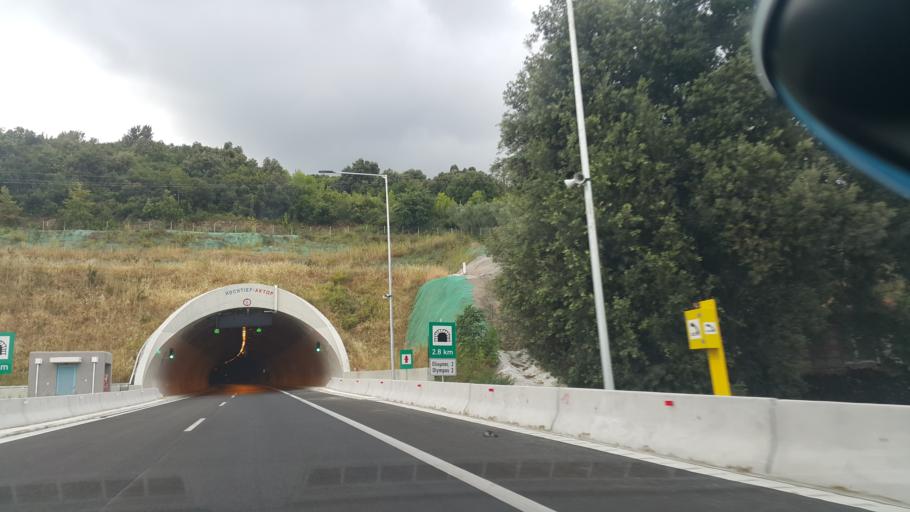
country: GR
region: Central Macedonia
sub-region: Nomos Pierias
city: Leptokarya
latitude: 40.0115
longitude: 22.5818
